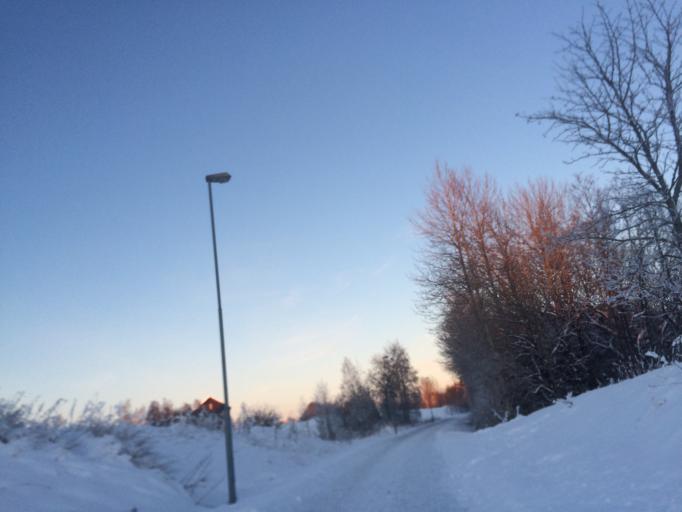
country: NO
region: Akershus
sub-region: Ski
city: Ski
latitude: 59.7035
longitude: 10.8326
